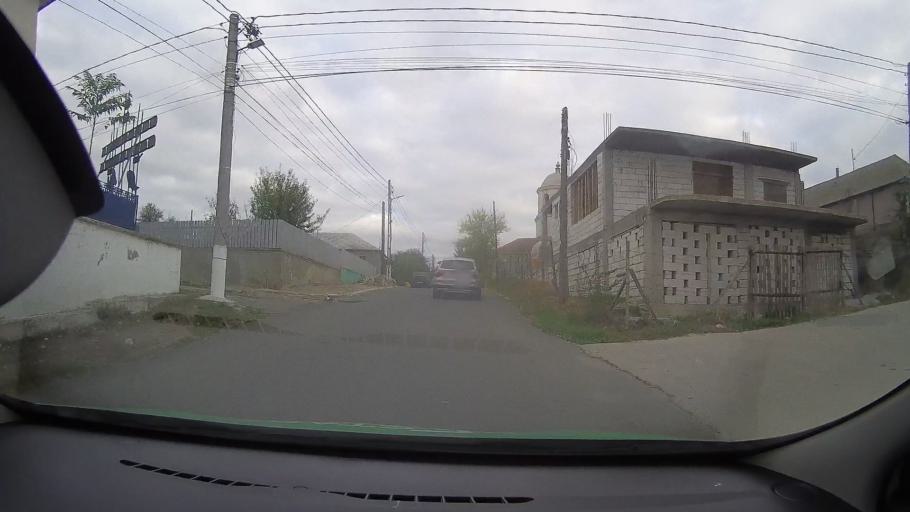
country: RO
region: Tulcea
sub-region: Comuna Jurilovca
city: Jurilovca
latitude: 44.7557
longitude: 28.8758
